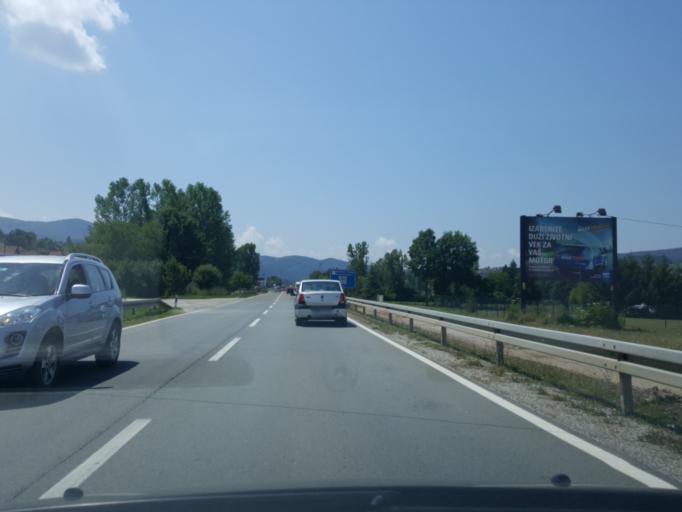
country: RS
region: Central Serbia
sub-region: Moravicki Okrug
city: Gornji Milanovac
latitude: 44.0295
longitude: 20.4716
